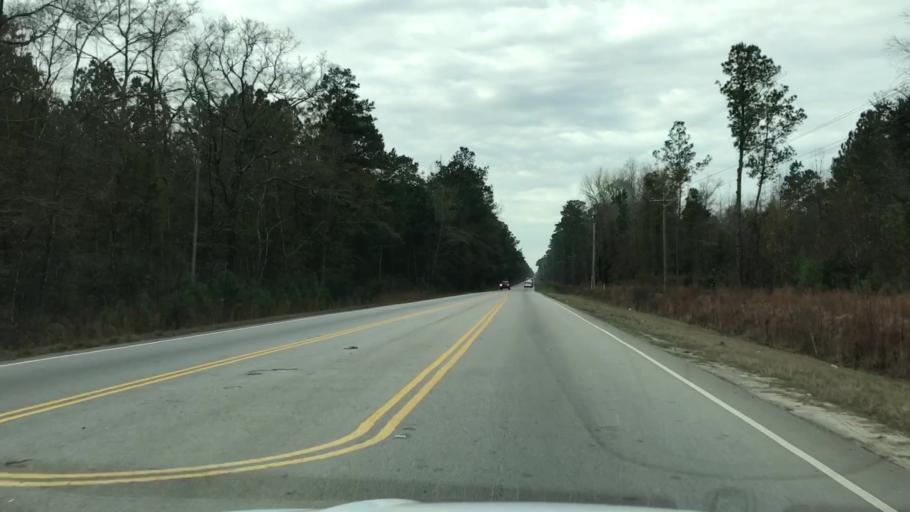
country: US
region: South Carolina
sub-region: Jasper County
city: Ridgeland
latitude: 32.3851
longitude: -80.9088
